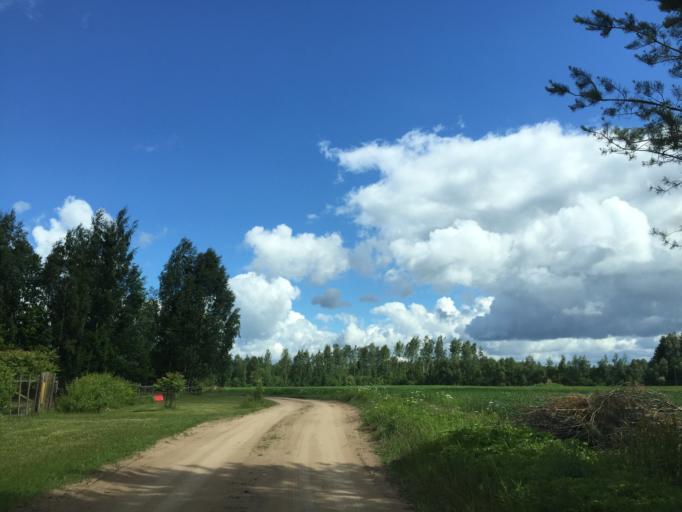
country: LV
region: Lecava
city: Iecava
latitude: 56.6836
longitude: 24.2557
